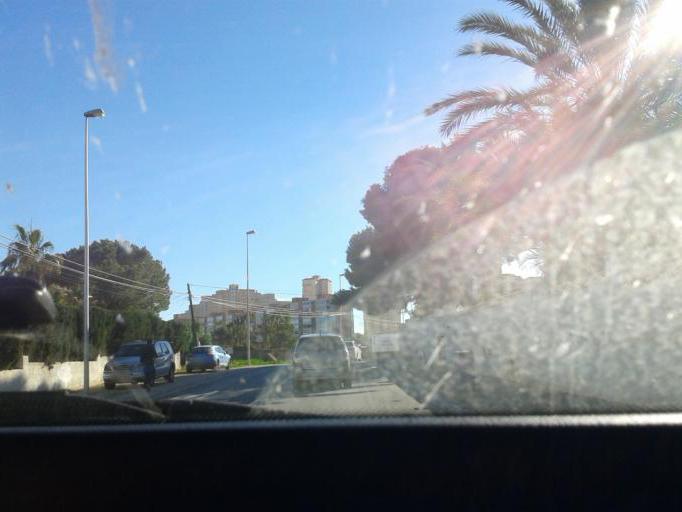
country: ES
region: Valencia
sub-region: Provincia de Alicante
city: el Campello
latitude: 38.4107
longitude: -0.4073
